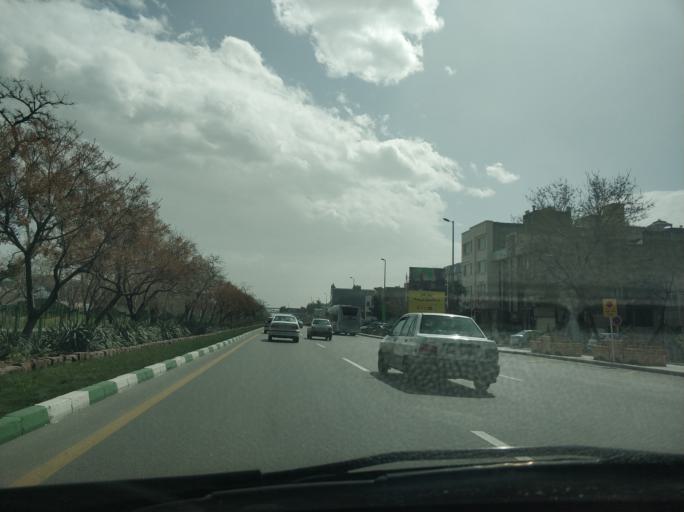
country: IR
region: Razavi Khorasan
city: Mashhad
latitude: 36.3221
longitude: 59.5178
